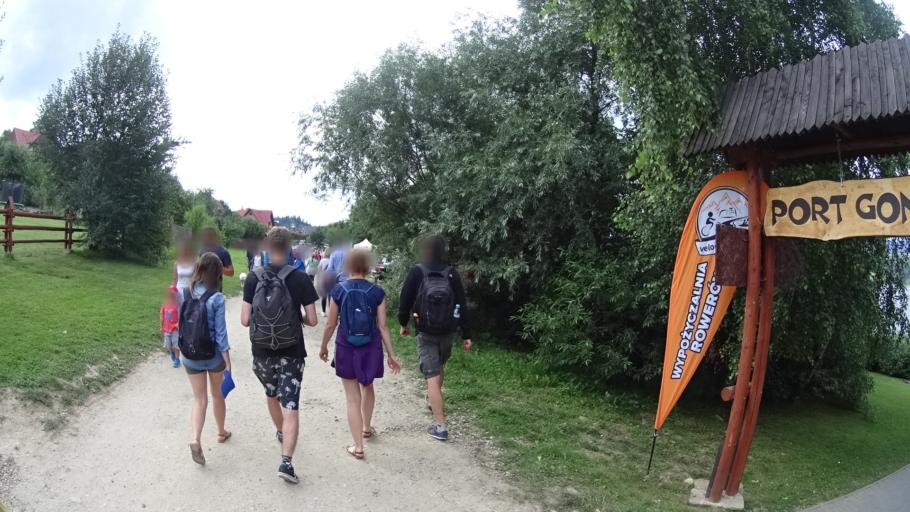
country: PL
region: Lesser Poland Voivodeship
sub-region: Powiat nowotarski
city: Niedzica
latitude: 49.4230
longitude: 20.3158
